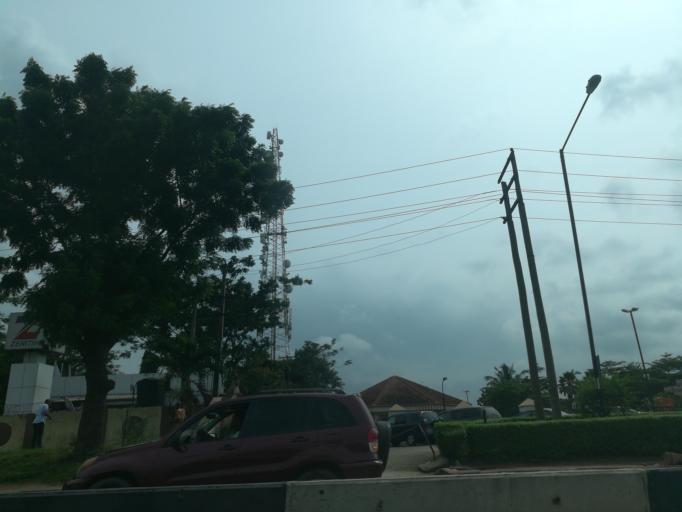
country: NG
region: Lagos
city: Ikeja
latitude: 6.6146
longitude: 3.3647
